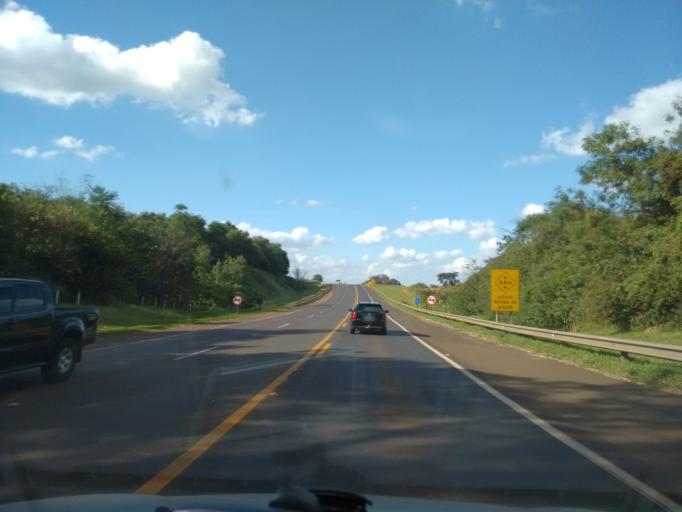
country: BR
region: Sao Paulo
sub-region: Americo Brasiliense
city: Americo Brasiliense
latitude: -21.7577
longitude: -48.0726
